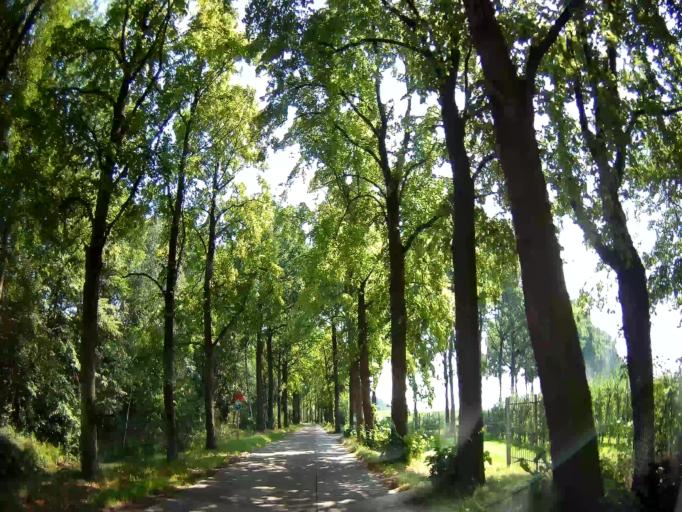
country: BE
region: Flanders
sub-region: Provincie Antwerpen
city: Oud-Turnhout
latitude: 51.2838
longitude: 5.0097
